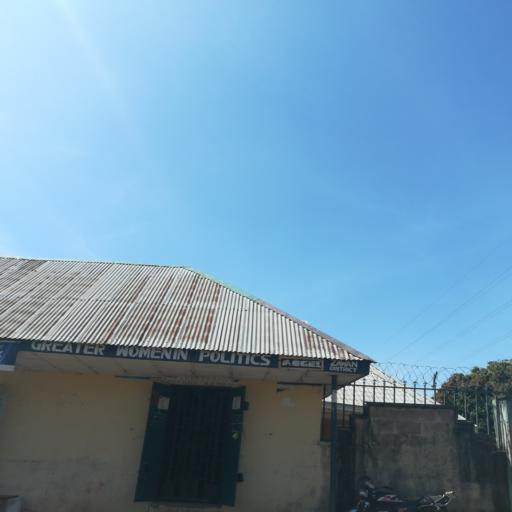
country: NG
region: Plateau
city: Bukuru
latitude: 9.7601
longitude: 8.8617
